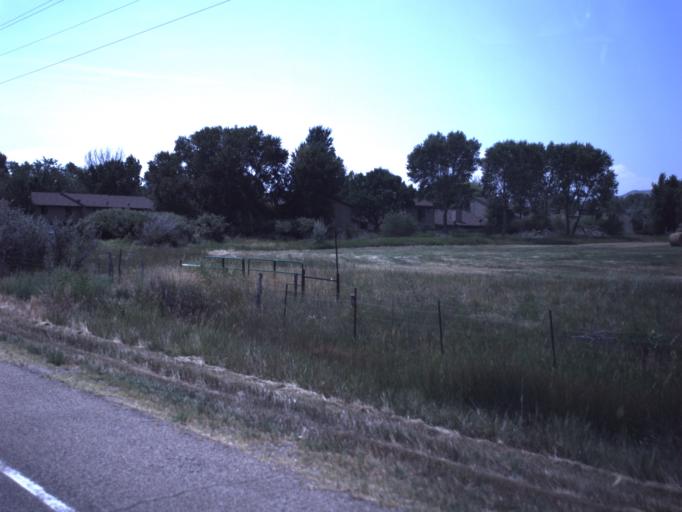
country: US
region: Utah
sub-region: Uintah County
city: Vernal
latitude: 40.4758
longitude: -109.5289
